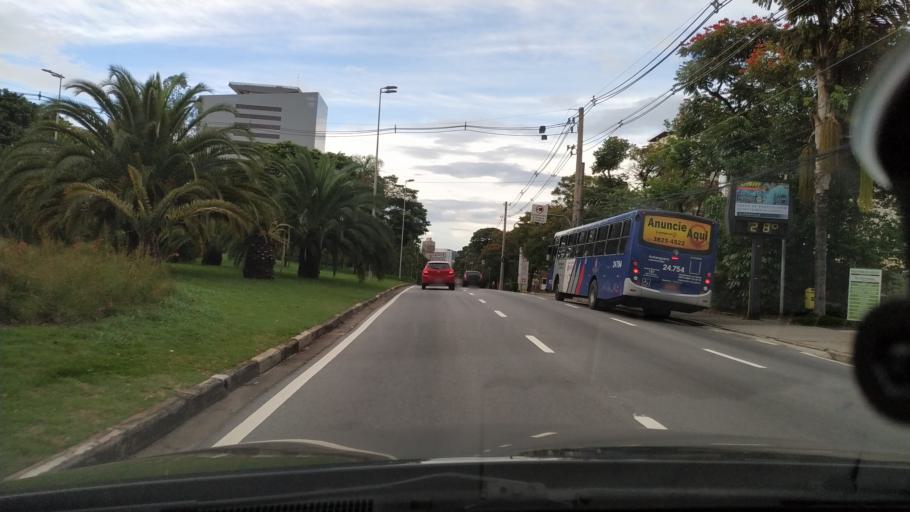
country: BR
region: Sao Paulo
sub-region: Carapicuiba
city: Carapicuiba
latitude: -23.4953
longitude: -46.8487
